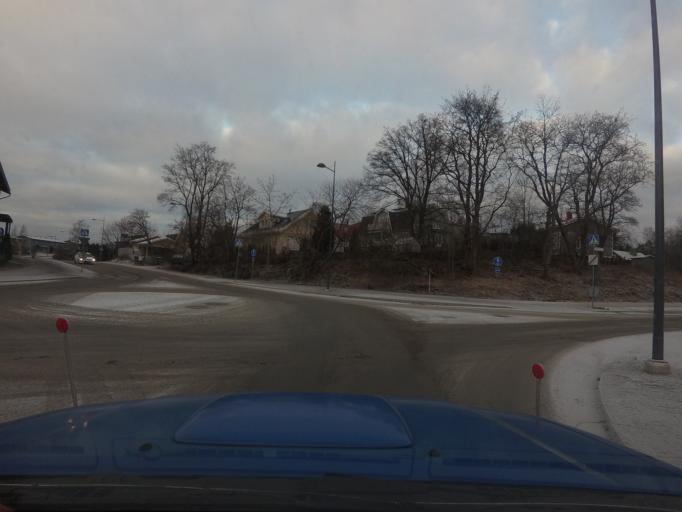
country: FI
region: Uusimaa
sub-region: Helsinki
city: Espoo
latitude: 60.1938
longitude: 24.6004
